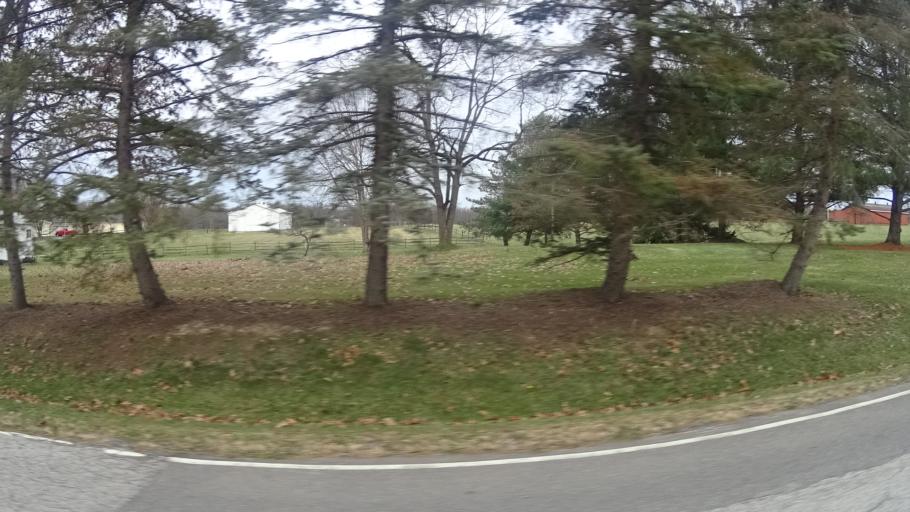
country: US
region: Ohio
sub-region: Cuyahoga County
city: Strongsville
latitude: 41.2895
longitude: -81.9036
